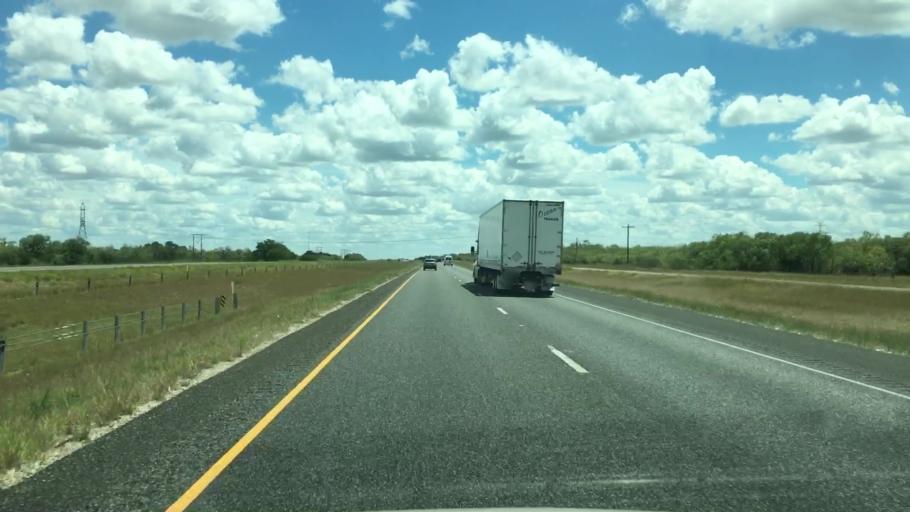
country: US
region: Texas
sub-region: Atascosa County
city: Pleasanton
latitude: 28.8269
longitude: -98.3665
